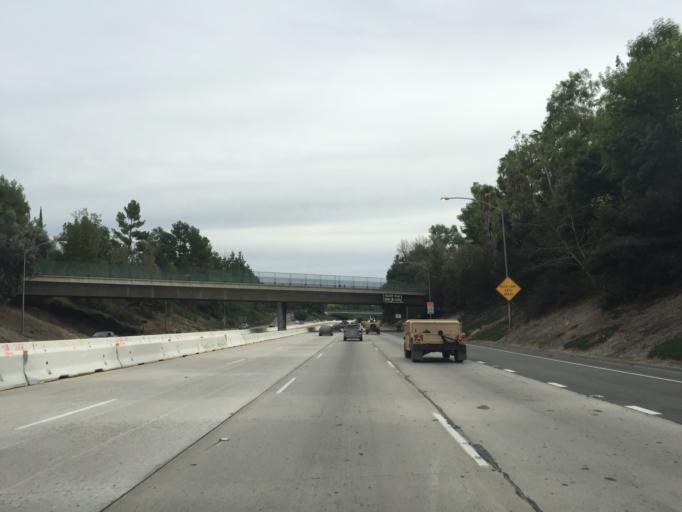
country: US
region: California
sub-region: Los Angeles County
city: La Canada Flintridge
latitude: 34.2044
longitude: -118.1950
